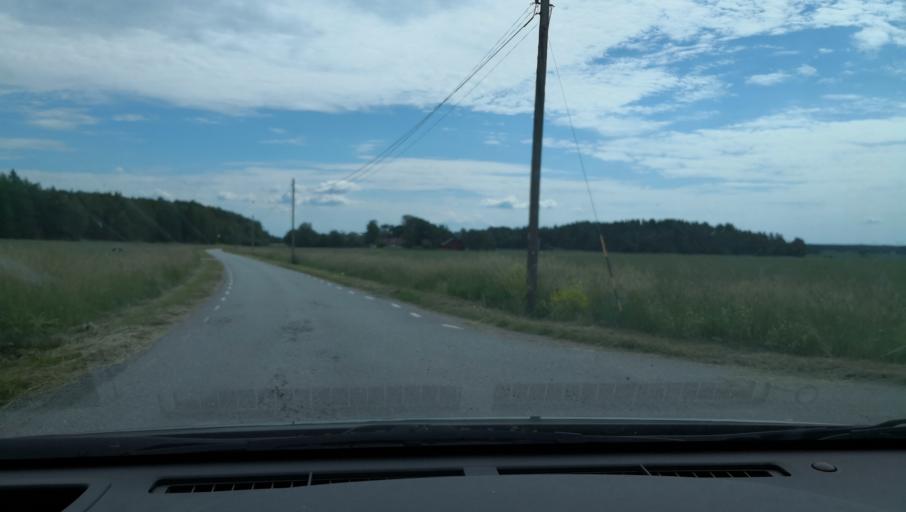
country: SE
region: Uppsala
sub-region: Enkopings Kommun
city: Orsundsbro
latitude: 59.6980
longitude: 17.4344
